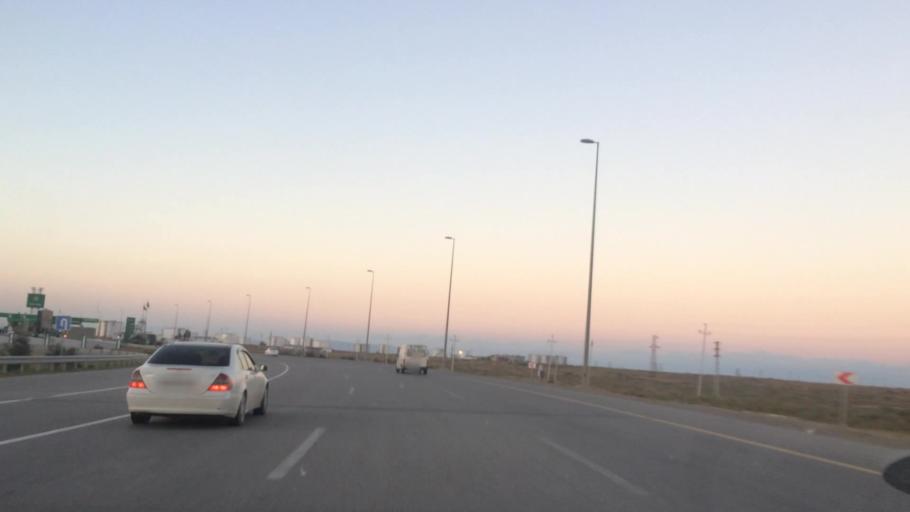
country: AZ
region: Baki
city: Qobustan
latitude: 39.9923
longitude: 49.4312
